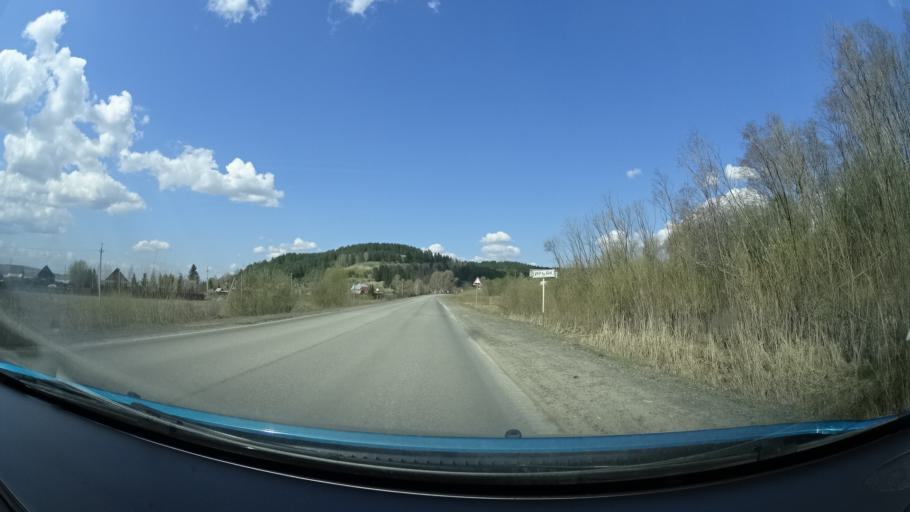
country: RU
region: Perm
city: Osa
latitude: 57.2205
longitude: 55.5901
